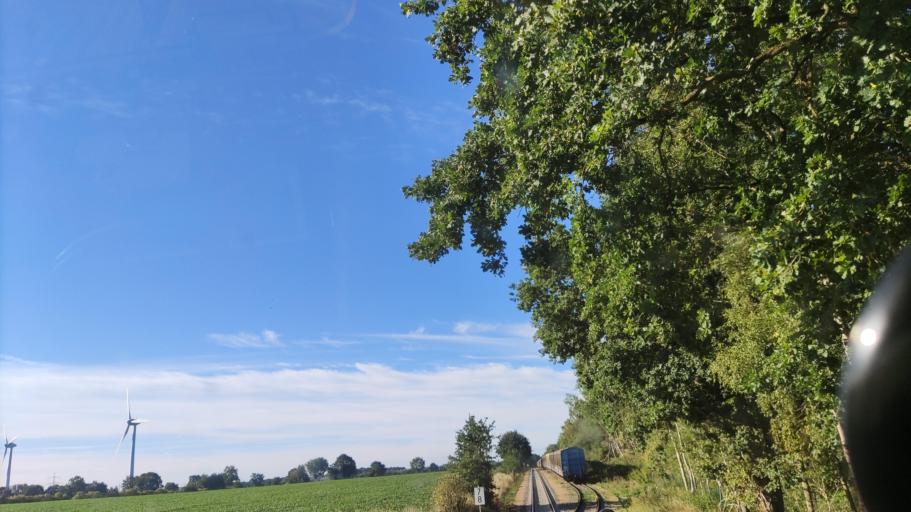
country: DE
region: Lower Saxony
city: Melbeck
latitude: 53.1942
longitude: 10.3776
